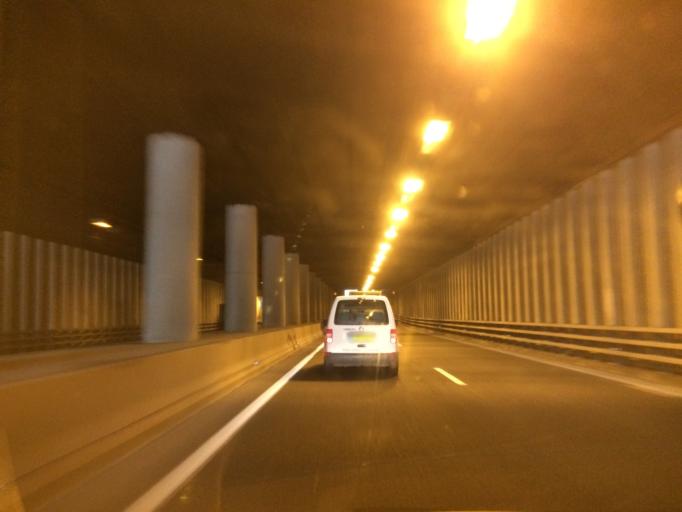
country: LU
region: Luxembourg
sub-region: Canton d'Esch-sur-Alzette
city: Mondercange
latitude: 49.5250
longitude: 5.9677
